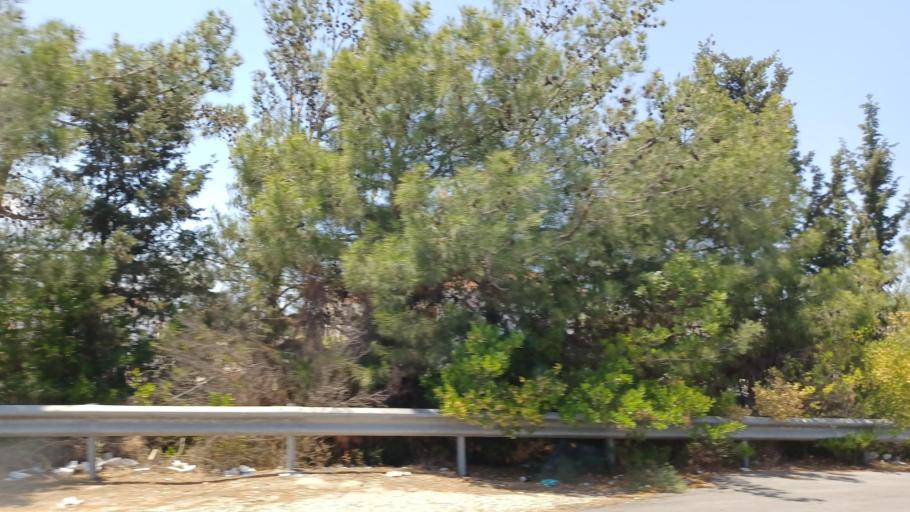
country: CY
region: Larnaka
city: Voroklini
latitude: 34.9797
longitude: 33.6790
